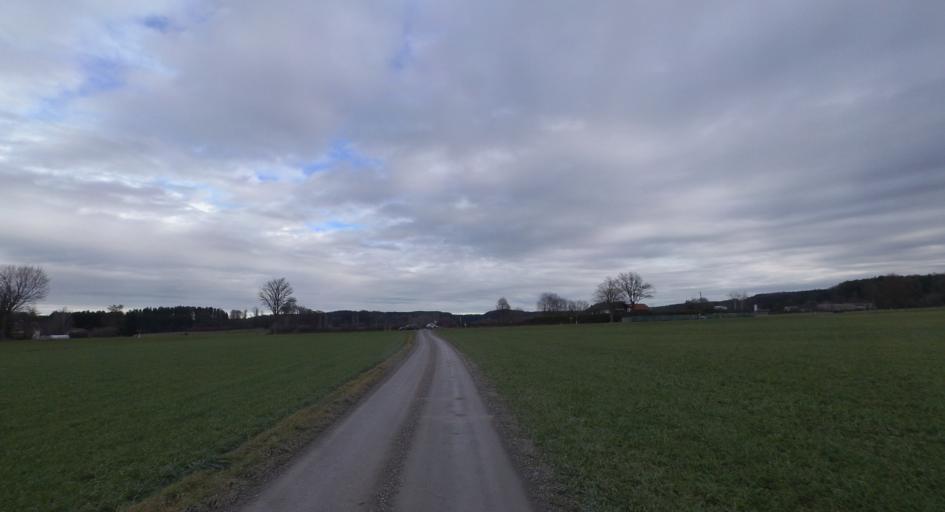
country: DE
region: Bavaria
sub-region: Upper Bavaria
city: Chieming
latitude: 47.8953
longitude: 12.5577
